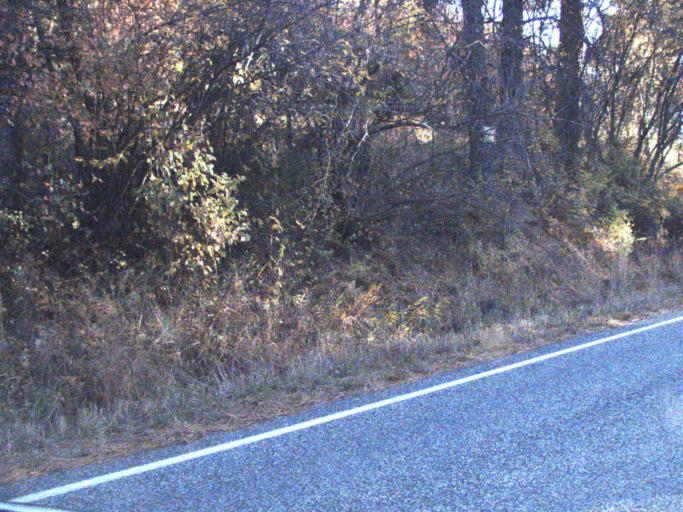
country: US
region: Washington
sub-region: Stevens County
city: Kettle Falls
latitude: 48.7560
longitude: -118.0414
